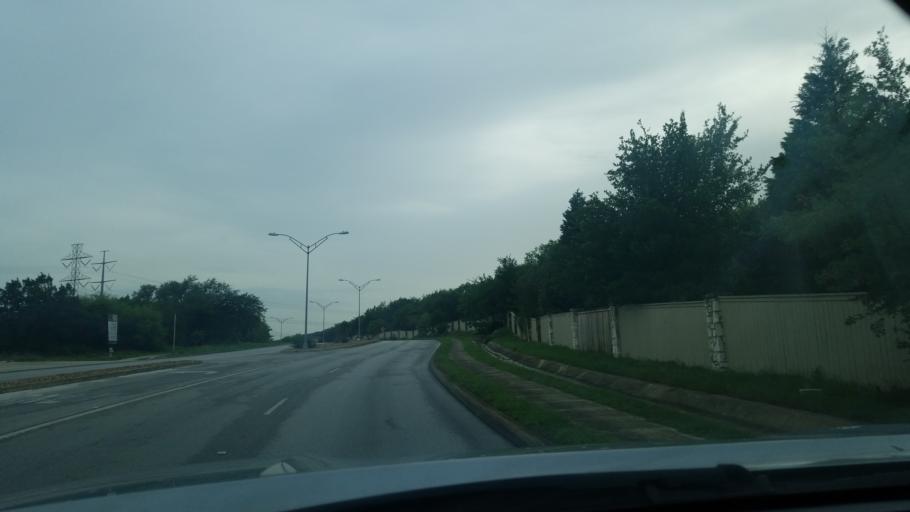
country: US
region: Texas
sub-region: Bexar County
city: Hollywood Park
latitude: 29.6203
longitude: -98.5143
